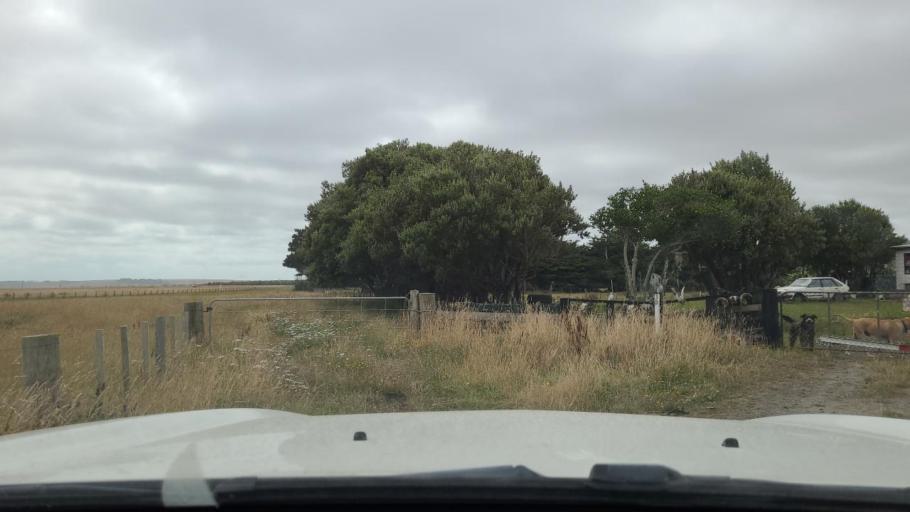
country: NZ
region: Chatham Islands
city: Waitangi
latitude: -43.9575
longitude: -176.5478
